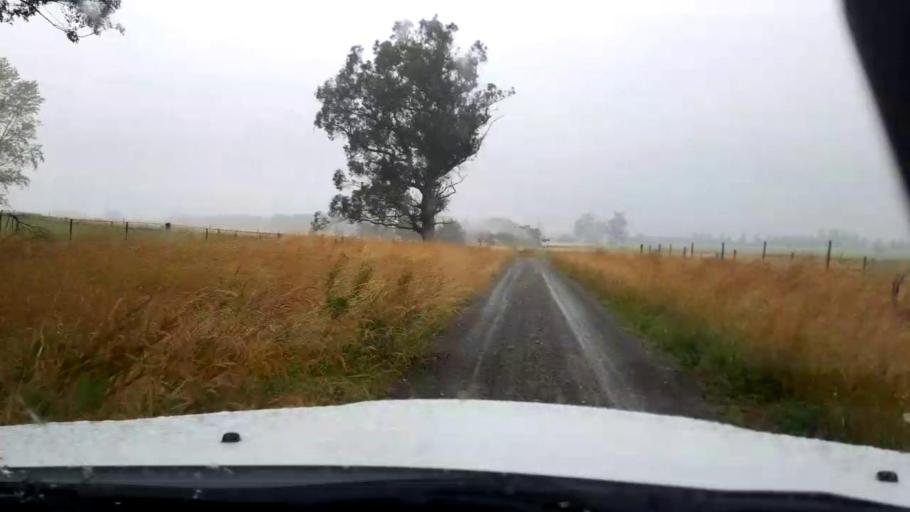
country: NZ
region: Canterbury
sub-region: Timaru District
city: Pleasant Point
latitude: -44.1953
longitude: 171.1044
